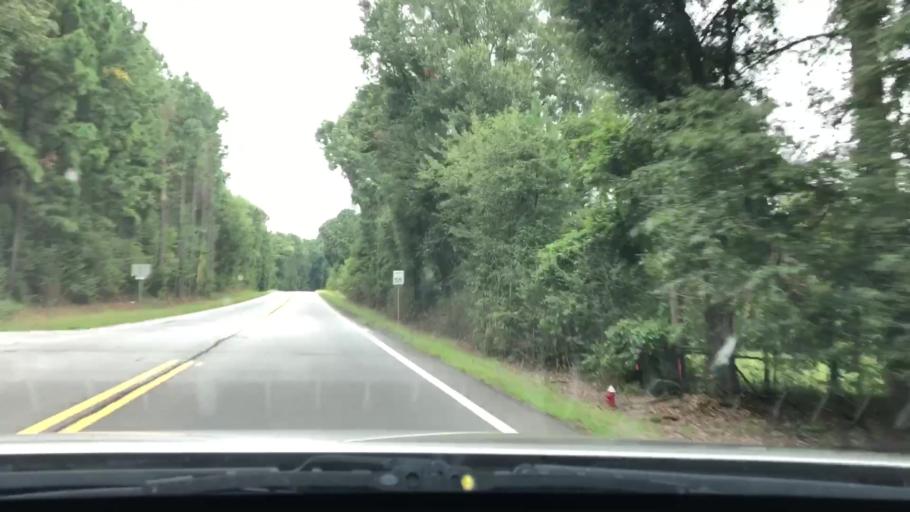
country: US
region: Georgia
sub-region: Upson County
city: Hannahs Mill
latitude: 33.0228
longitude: -84.4972
